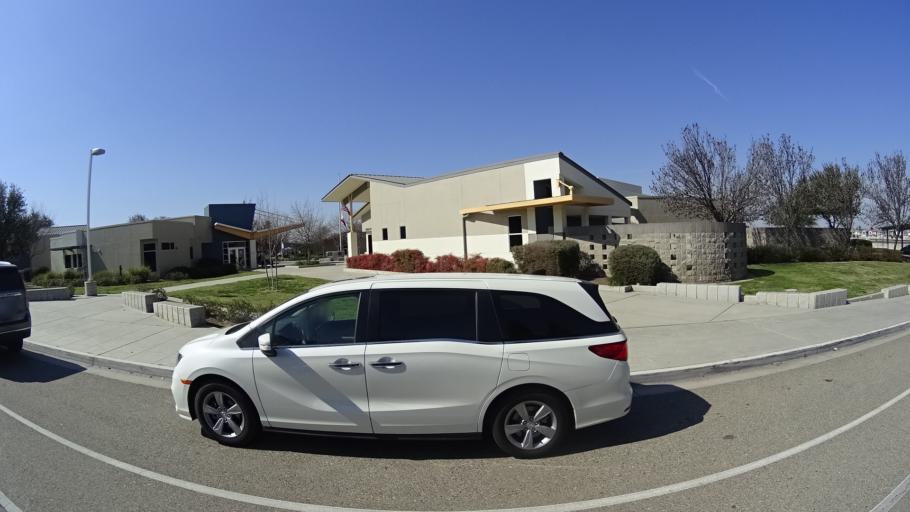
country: US
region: California
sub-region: Fresno County
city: Clovis
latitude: 36.8929
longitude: -119.7565
